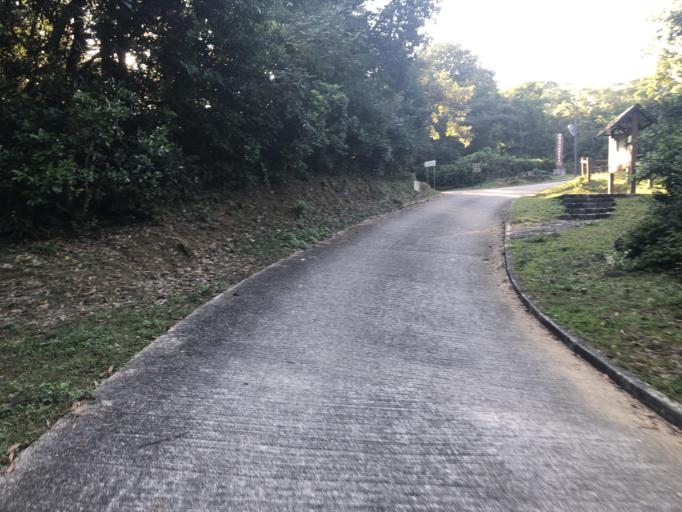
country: HK
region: Tsuen Wan
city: Tsuen Wan
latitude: 22.3964
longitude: 114.0747
